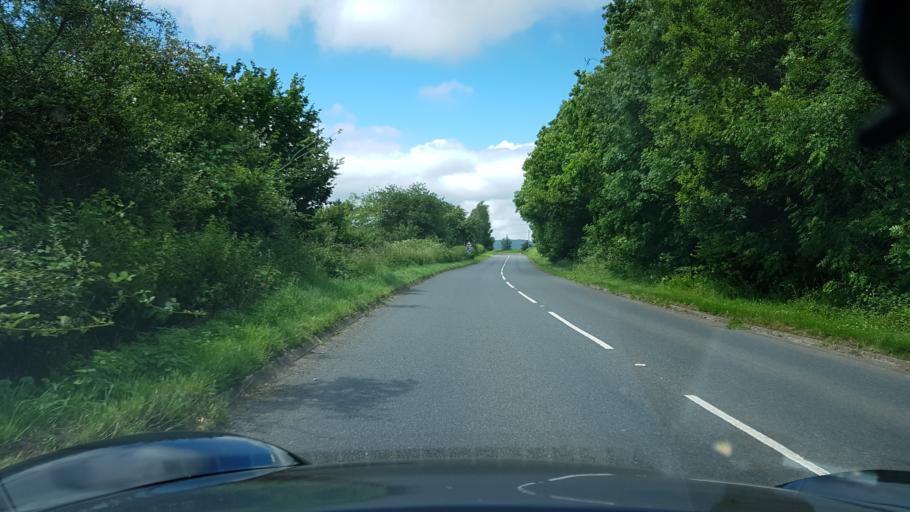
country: GB
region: Wales
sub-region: Monmouthshire
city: Abergavenny
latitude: 51.7933
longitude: -2.9918
